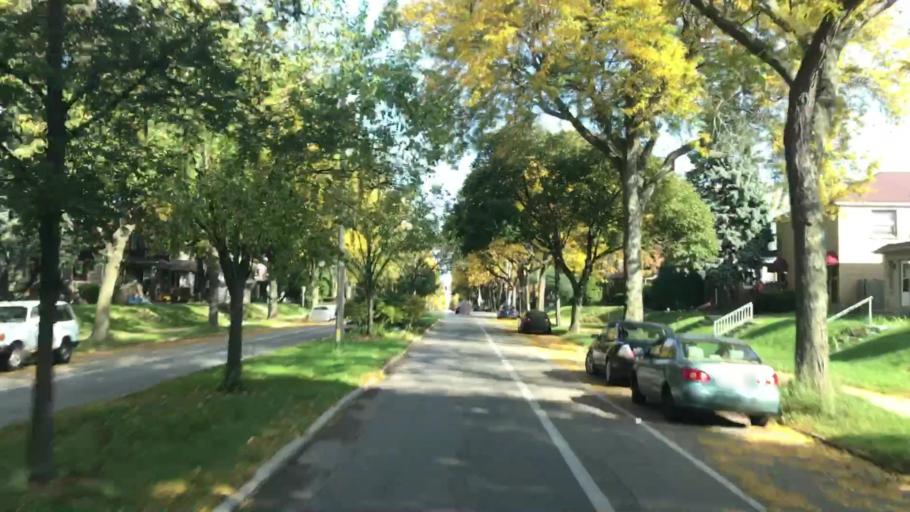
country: US
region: Wisconsin
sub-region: Milwaukee County
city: Shorewood
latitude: 43.0809
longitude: -87.8975
